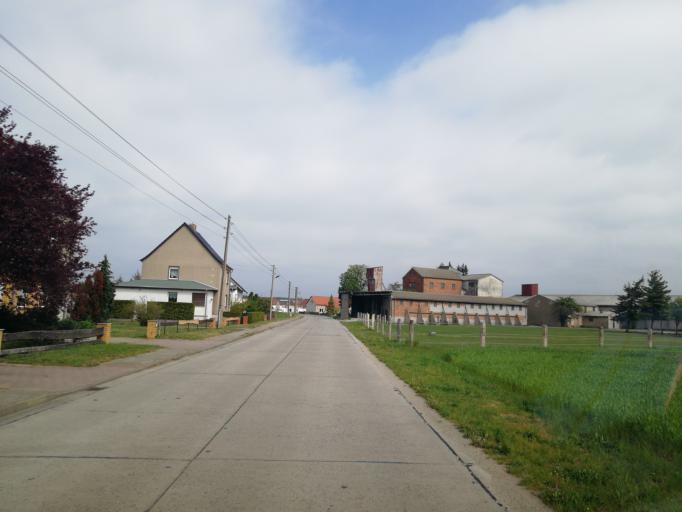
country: DE
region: Saxony
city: Beilrode
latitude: 51.6454
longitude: 13.1193
